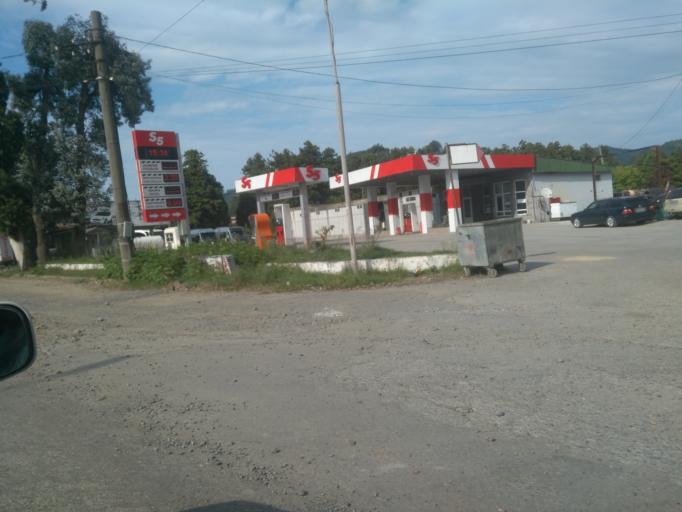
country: GE
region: Ajaria
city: Khelvachauri
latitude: 41.5893
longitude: 41.6478
